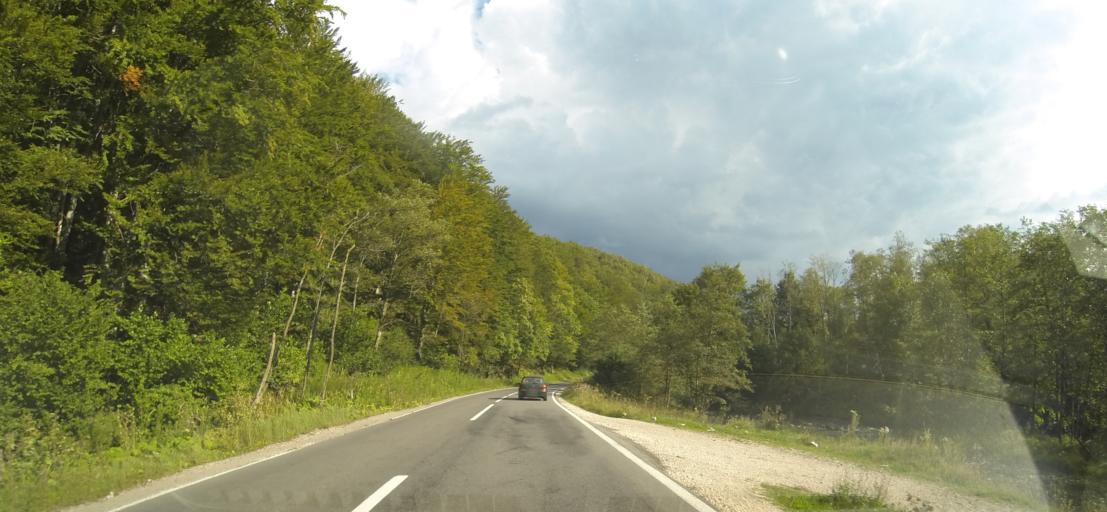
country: RO
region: Brasov
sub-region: Comuna Tarlungeni
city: Zizin
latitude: 45.5213
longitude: 25.8434
